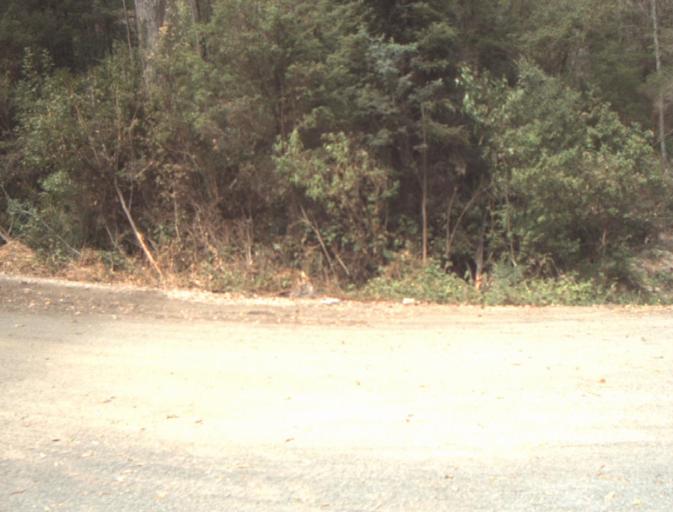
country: AU
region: Tasmania
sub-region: Launceston
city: Mayfield
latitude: -41.2132
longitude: 147.2122
